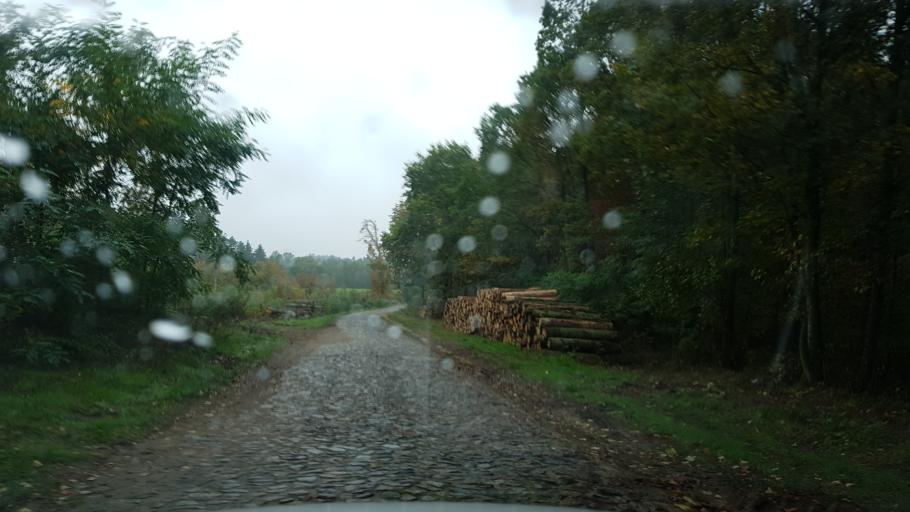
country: PL
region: West Pomeranian Voivodeship
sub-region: Powiat mysliborski
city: Barlinek
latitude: 53.0305
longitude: 15.2314
